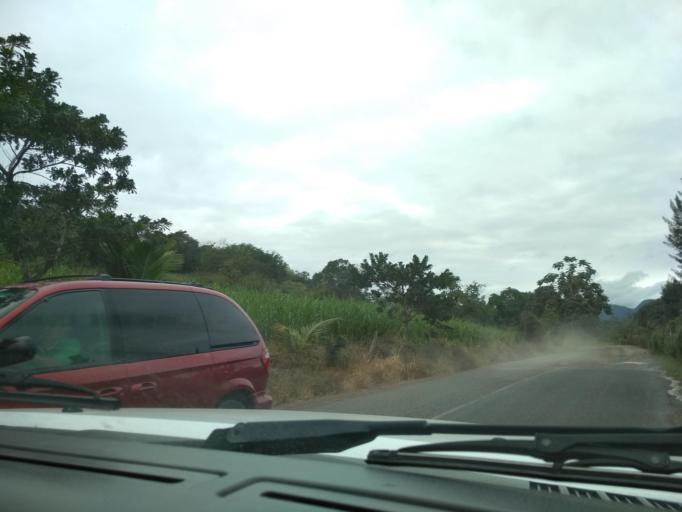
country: MX
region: Veracruz
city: Alto Lucero
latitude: 19.5990
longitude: -96.7955
